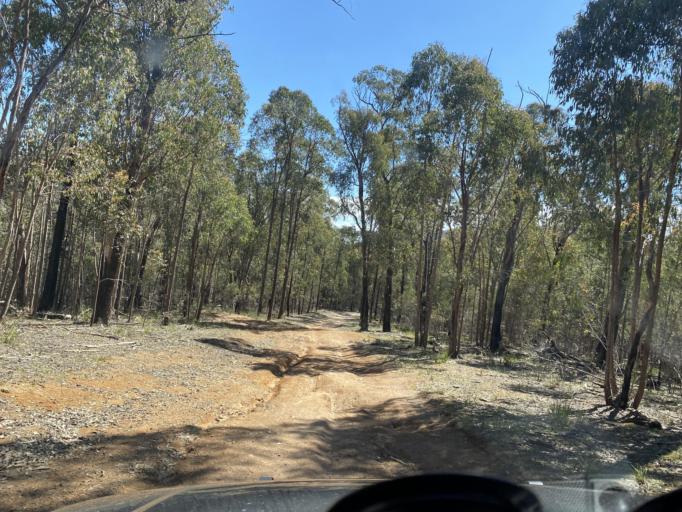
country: AU
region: Victoria
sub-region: Benalla
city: Benalla
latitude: -36.7156
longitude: 146.1812
